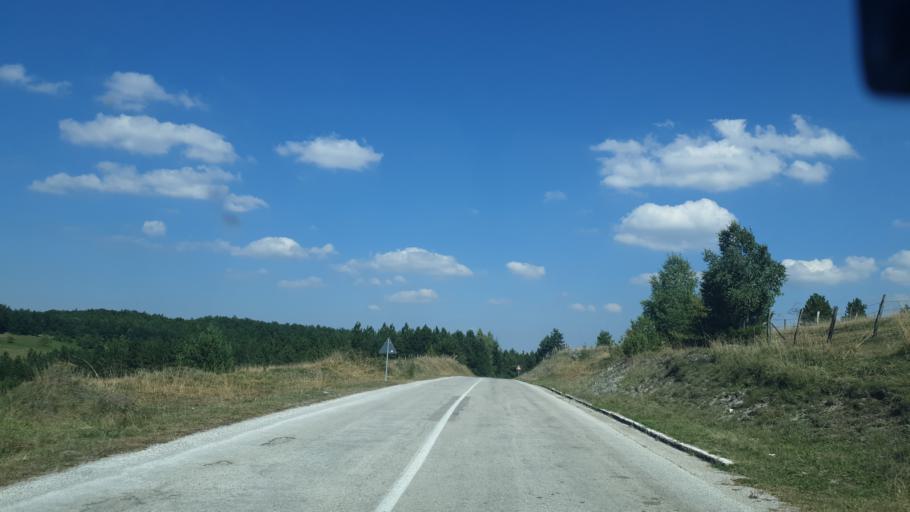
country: RS
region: Central Serbia
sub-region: Zlatiborski Okrug
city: Kosjeric
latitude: 44.0261
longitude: 20.0141
